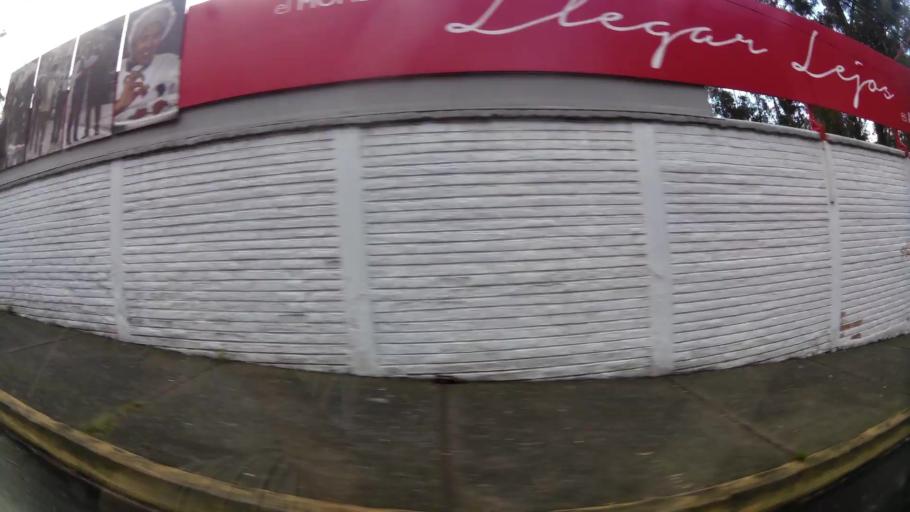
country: EC
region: Pichincha
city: Quito
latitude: -0.1119
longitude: -78.5022
